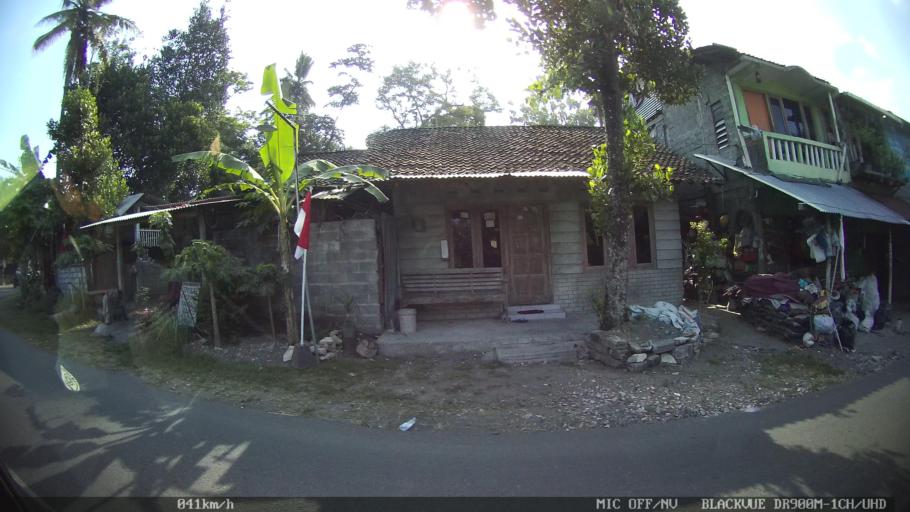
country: ID
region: Daerah Istimewa Yogyakarta
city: Bantul
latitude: -7.8794
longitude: 110.3141
